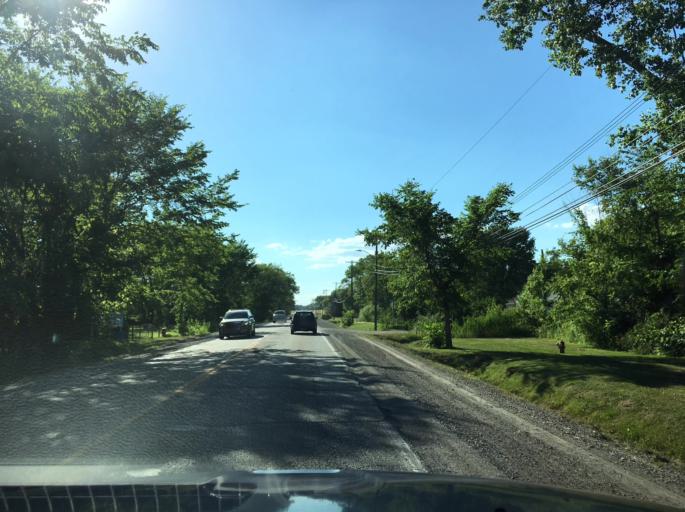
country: US
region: Michigan
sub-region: Macomb County
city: Fraser
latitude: 42.5708
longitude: -82.9742
